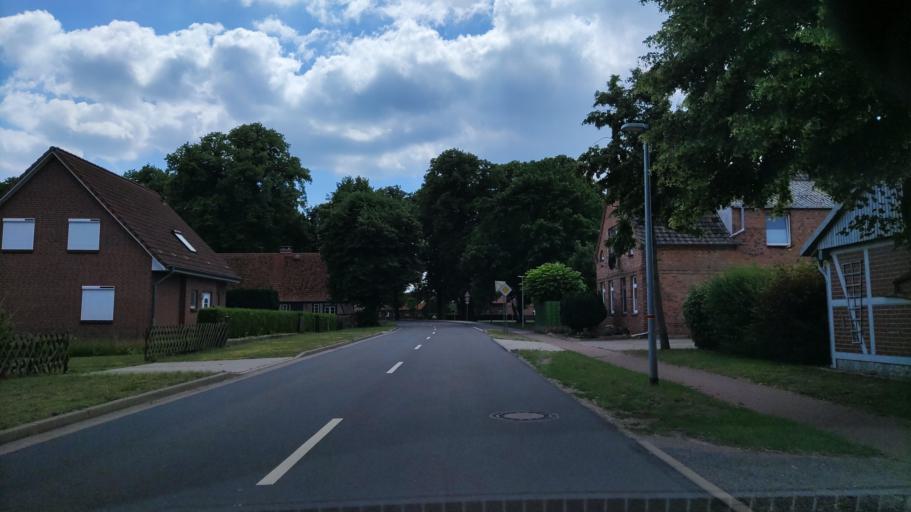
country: DE
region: Mecklenburg-Vorpommern
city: Hagenow
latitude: 53.3800
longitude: 11.1508
